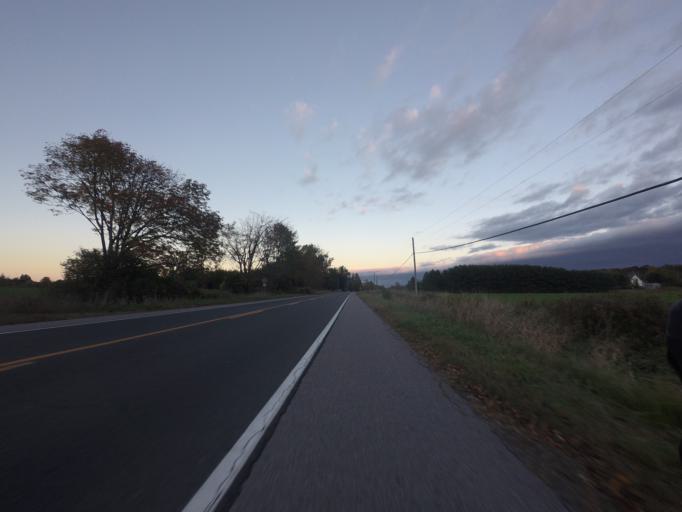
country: CA
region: Ontario
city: Quinte West
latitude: 44.0378
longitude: -77.6942
